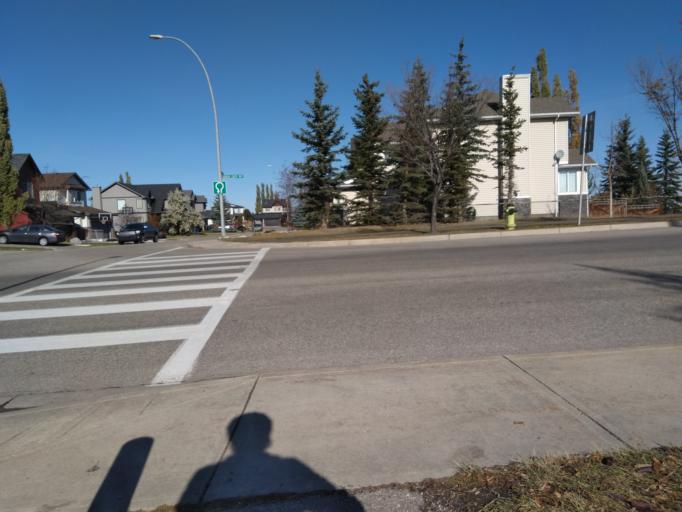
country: CA
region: Alberta
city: Calgary
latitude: 51.1597
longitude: -114.0971
